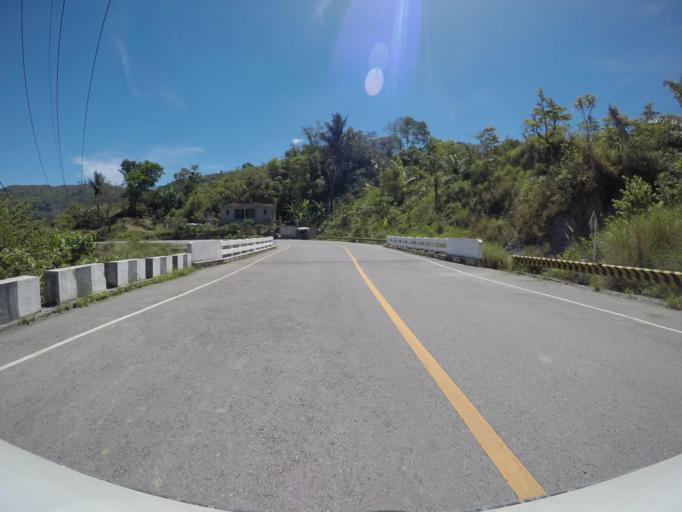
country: TL
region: Manatuto
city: Manatuto
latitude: -8.7785
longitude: 125.9681
